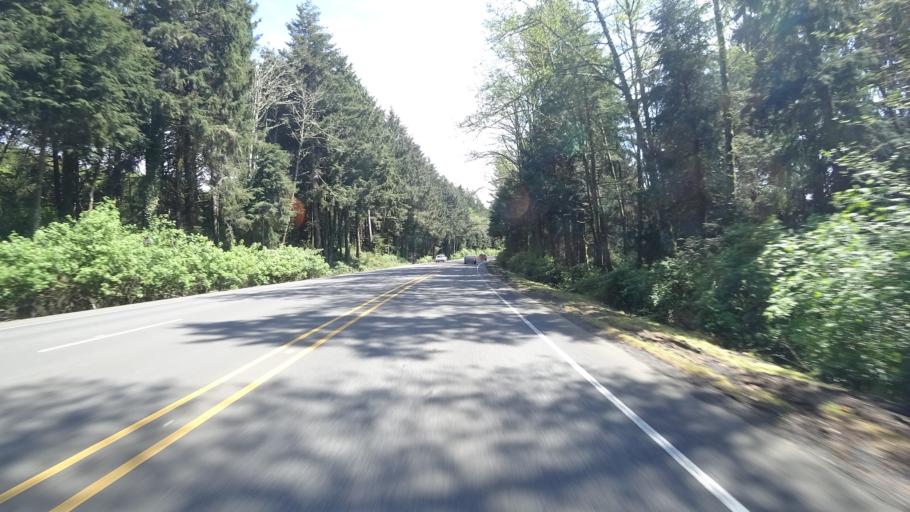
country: US
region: Oregon
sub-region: Lincoln County
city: Depoe Bay
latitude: 44.7515
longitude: -124.0528
